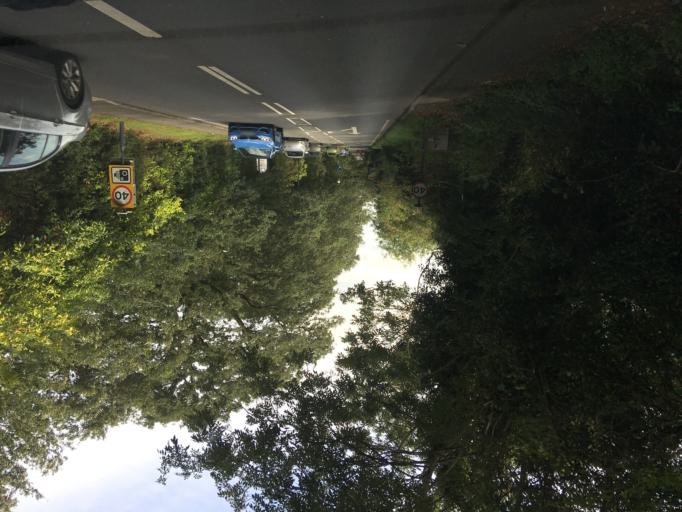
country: GB
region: England
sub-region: Warwickshire
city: Royal Leamington Spa
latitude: 52.3039
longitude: -1.5374
